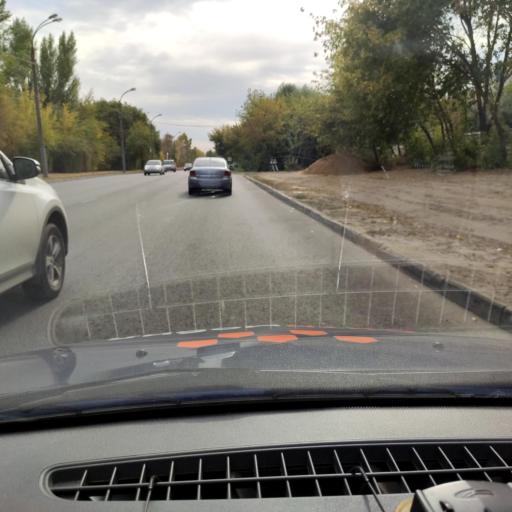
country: RU
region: Voronezj
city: Voronezh
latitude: 51.6428
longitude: 39.2108
